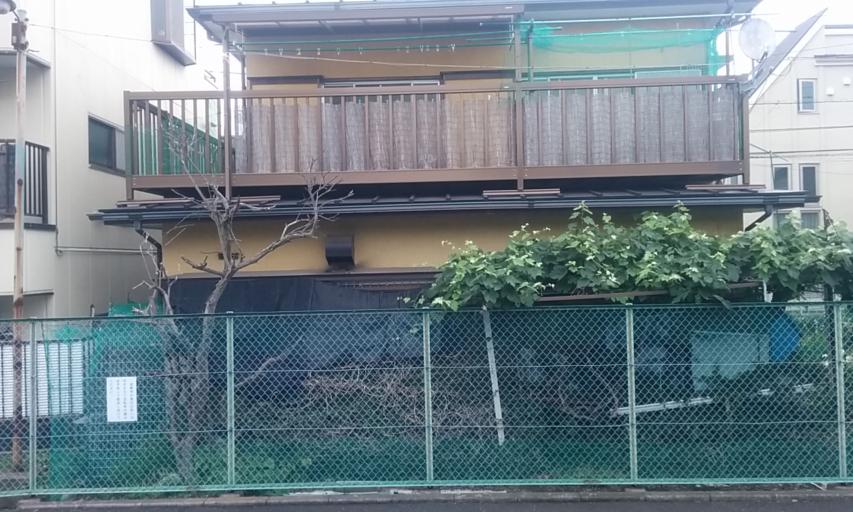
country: JP
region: Chiba
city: Nagareyama
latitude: 35.8412
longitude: 139.9110
